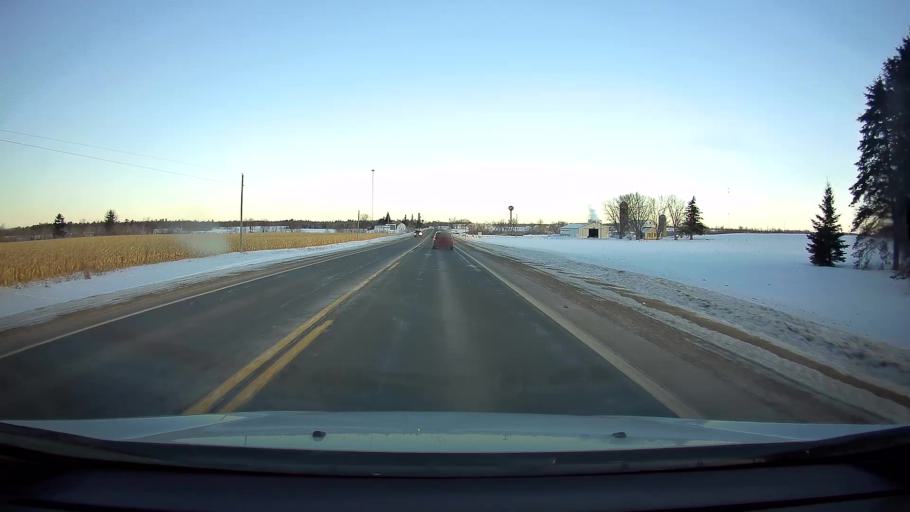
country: US
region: Wisconsin
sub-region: Barron County
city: Turtle Lake
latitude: 45.3812
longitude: -92.1667
